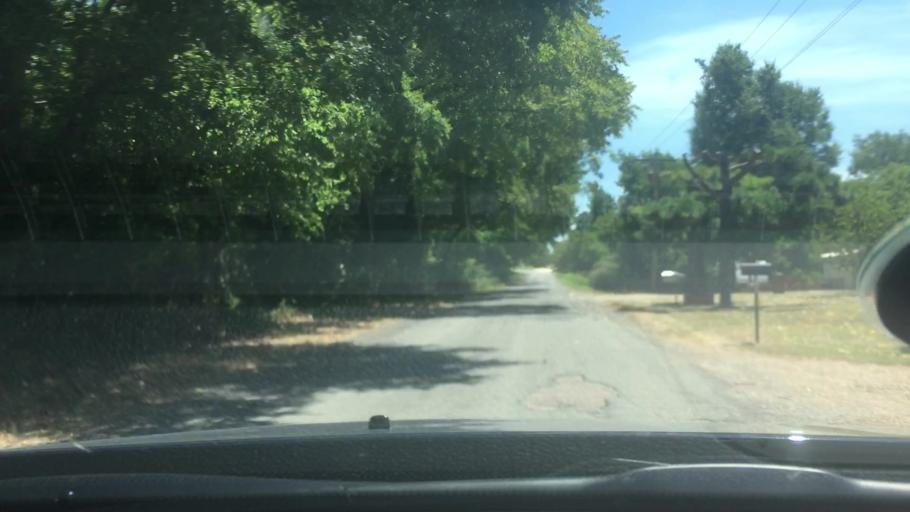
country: US
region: Oklahoma
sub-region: Bryan County
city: Durant
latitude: 33.9829
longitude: -96.2372
